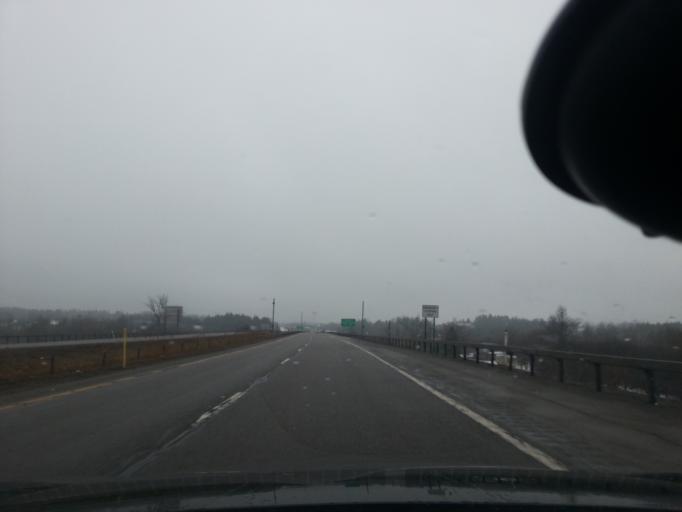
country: US
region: New York
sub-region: Jefferson County
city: Watertown
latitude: 43.9985
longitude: -75.9285
